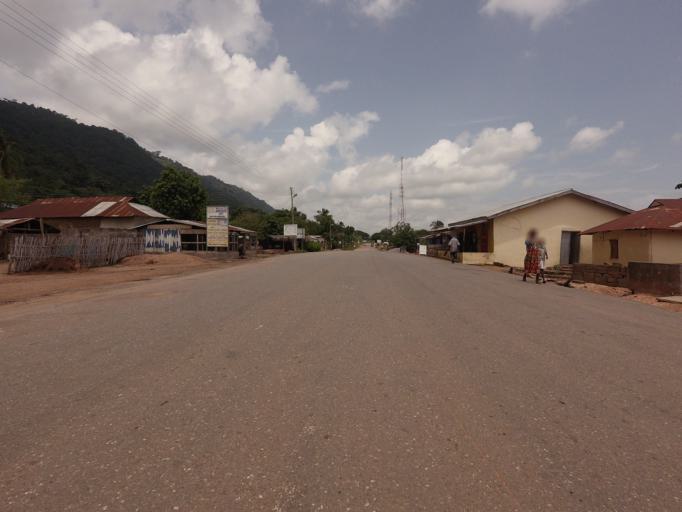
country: GH
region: Volta
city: Ho
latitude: 6.7601
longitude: 0.3618
